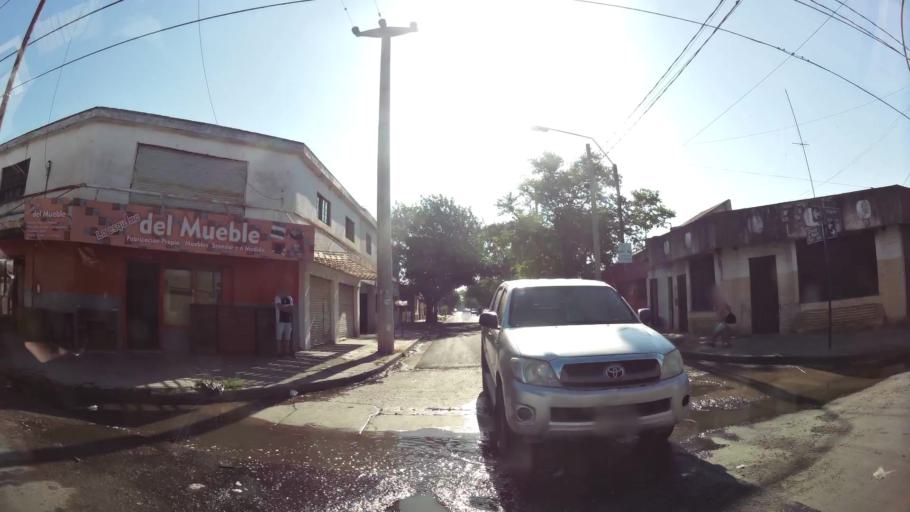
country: AR
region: Cordoba
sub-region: Departamento de Capital
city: Cordoba
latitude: -31.4710
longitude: -64.2243
